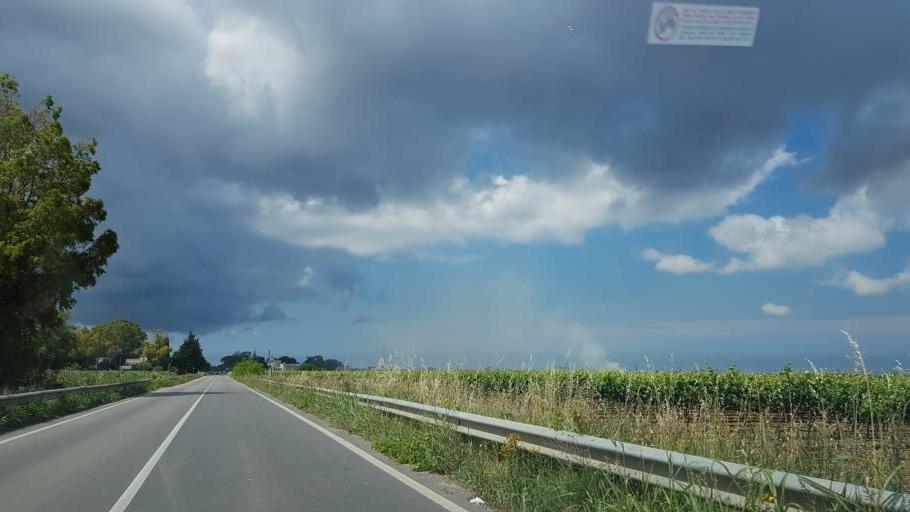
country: IT
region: Apulia
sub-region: Provincia di Brindisi
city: La Rosa
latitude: 40.5792
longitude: 17.9651
